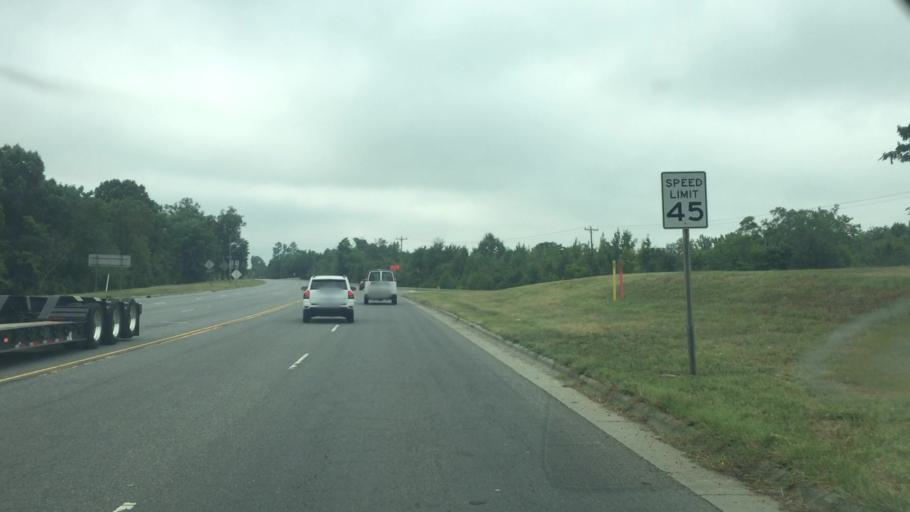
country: US
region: North Carolina
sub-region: Cabarrus County
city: Kannapolis
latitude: 35.4359
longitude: -80.6806
